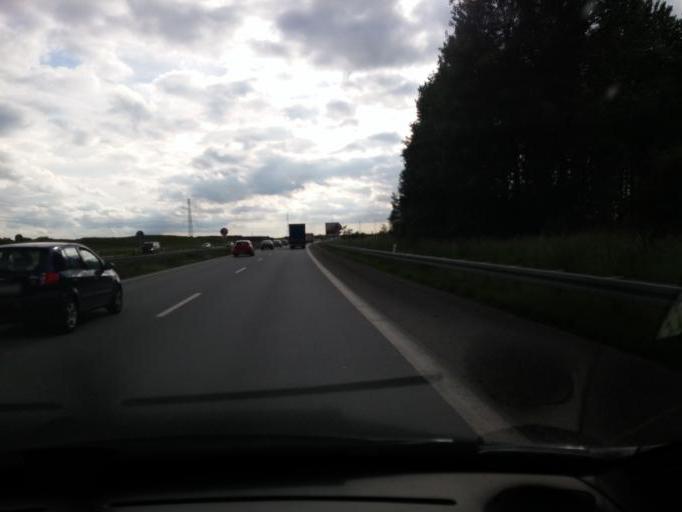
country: DK
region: Zealand
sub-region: Ringsted Kommune
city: Ringsted
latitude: 55.4551
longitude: 11.8233
